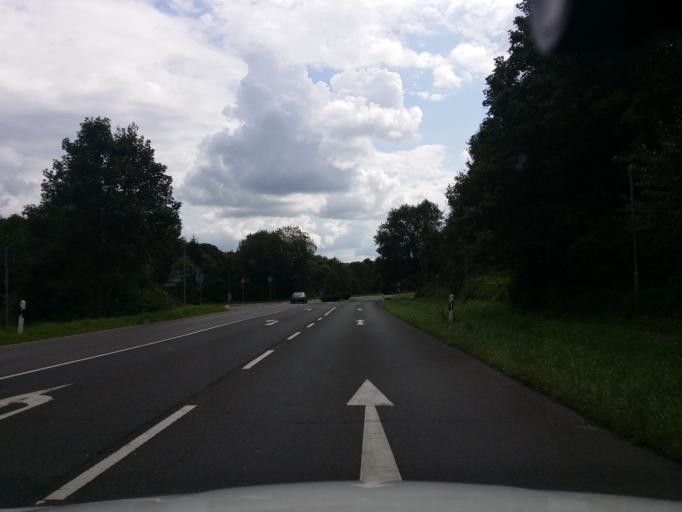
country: DE
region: Hesse
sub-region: Regierungsbezirk Darmstadt
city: Niedernhausen
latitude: 50.1587
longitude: 8.3210
